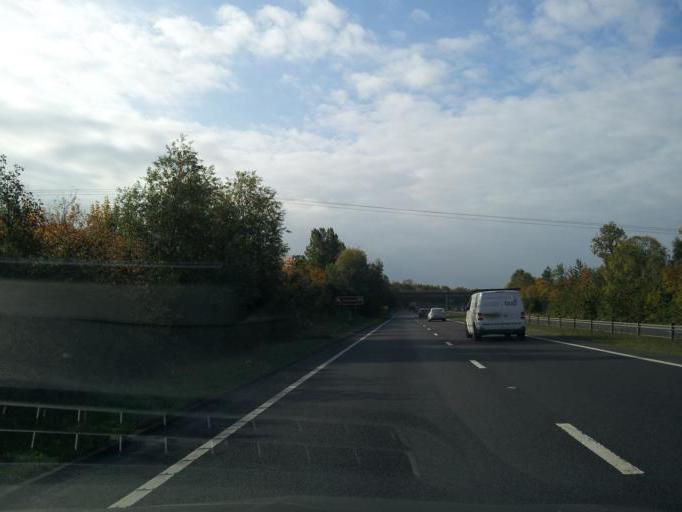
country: GB
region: England
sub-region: Northamptonshire
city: Silverstone
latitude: 52.0870
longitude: -1.0194
